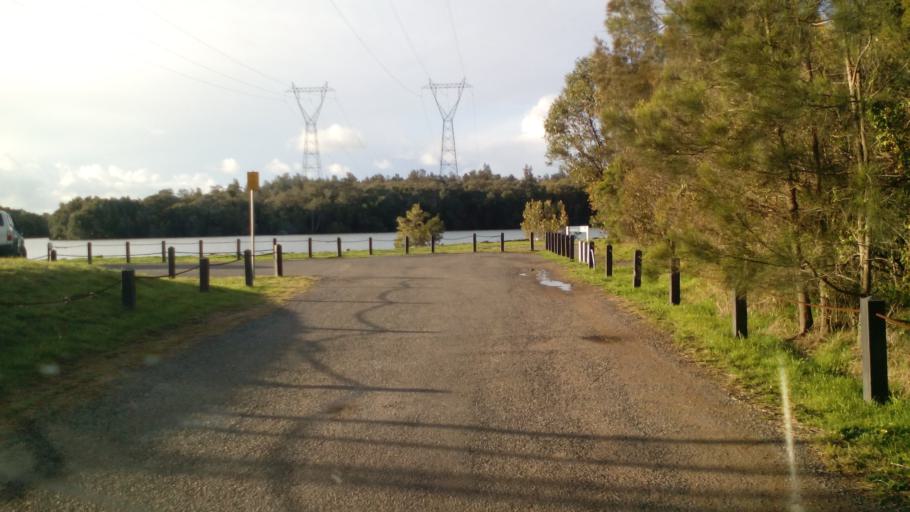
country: AU
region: New South Wales
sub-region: Newcastle
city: Mayfield West
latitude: -32.8343
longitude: 151.7088
